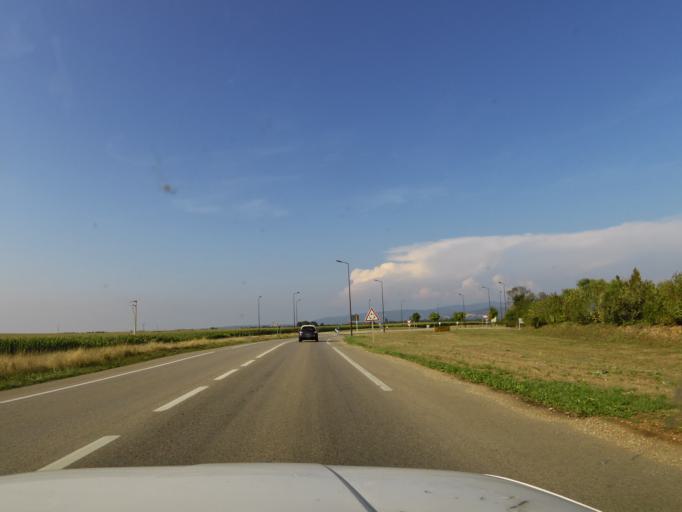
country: FR
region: Rhone-Alpes
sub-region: Departement de l'Isere
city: Hieres-sur-Amby
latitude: 45.8112
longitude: 5.2710
